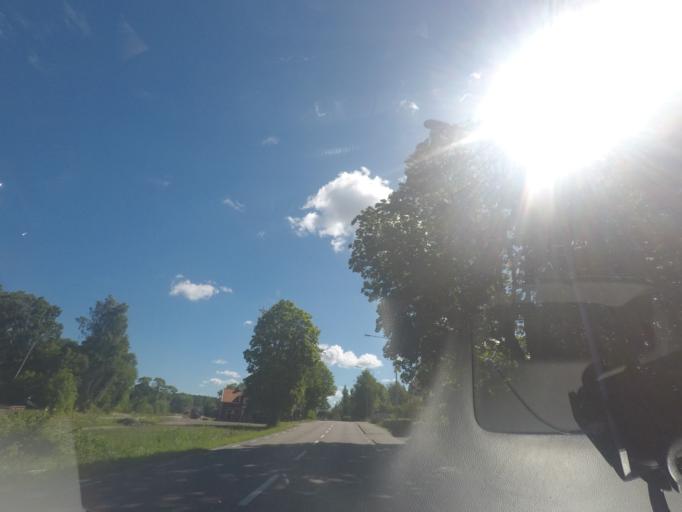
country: SE
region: Stockholm
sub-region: Norrtalje Kommun
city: Nykvarn
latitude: 59.8758
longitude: 18.0426
